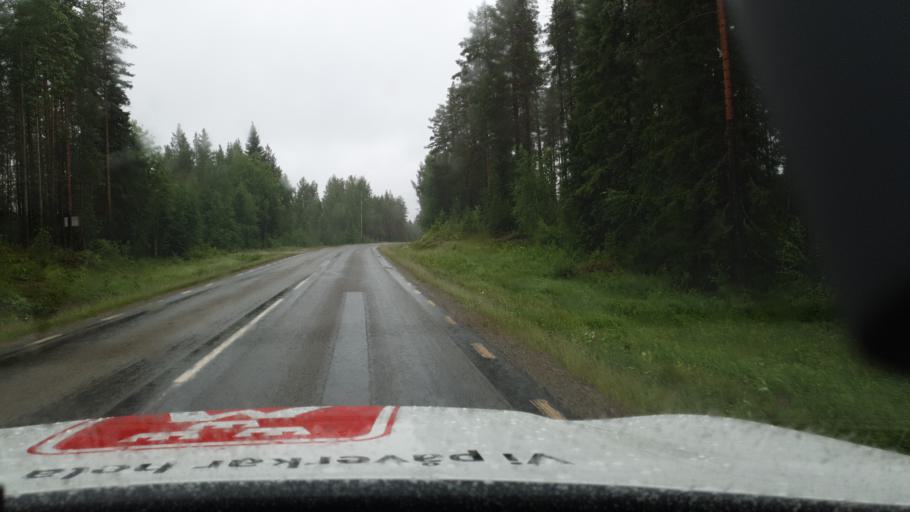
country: SE
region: Vaesterbotten
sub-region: Lycksele Kommun
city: Lycksele
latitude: 64.5014
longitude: 18.8975
